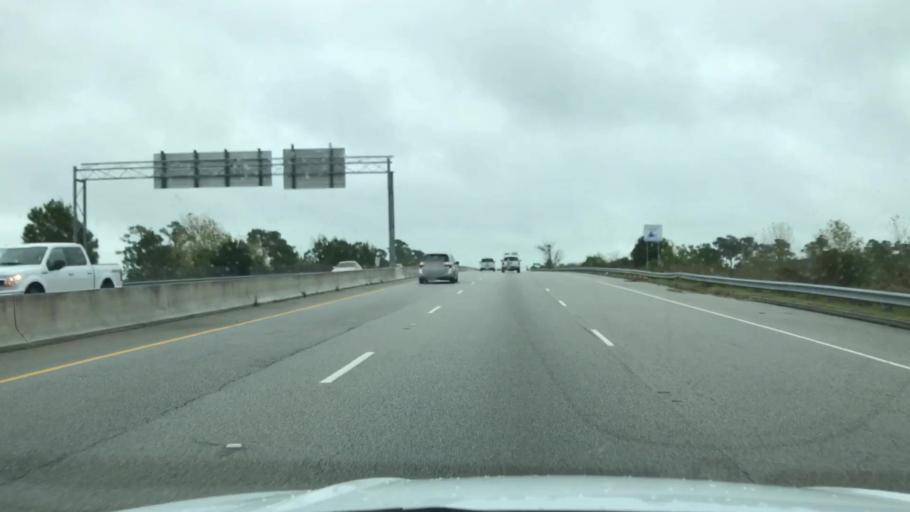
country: US
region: South Carolina
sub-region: Horry County
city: Myrtle Beach
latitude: 33.7518
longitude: -78.8509
